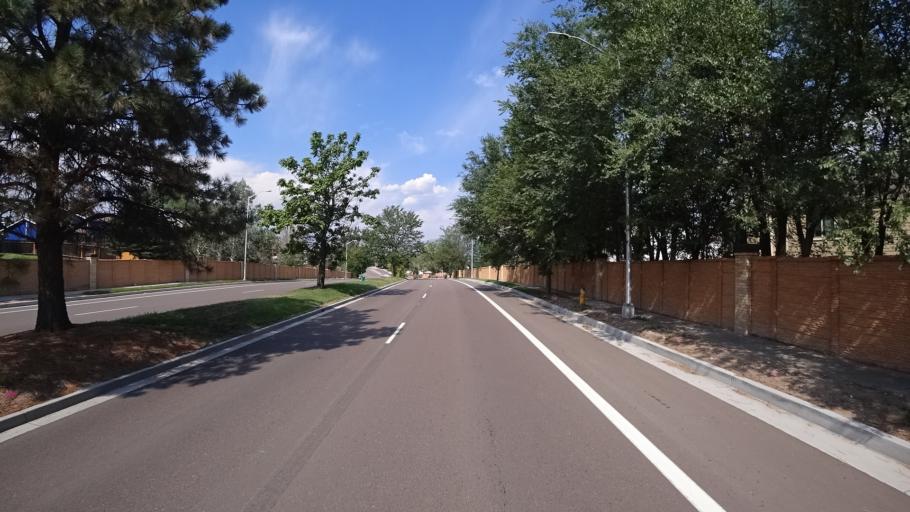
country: US
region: Colorado
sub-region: El Paso County
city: Cimarron Hills
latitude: 38.9253
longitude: -104.7632
